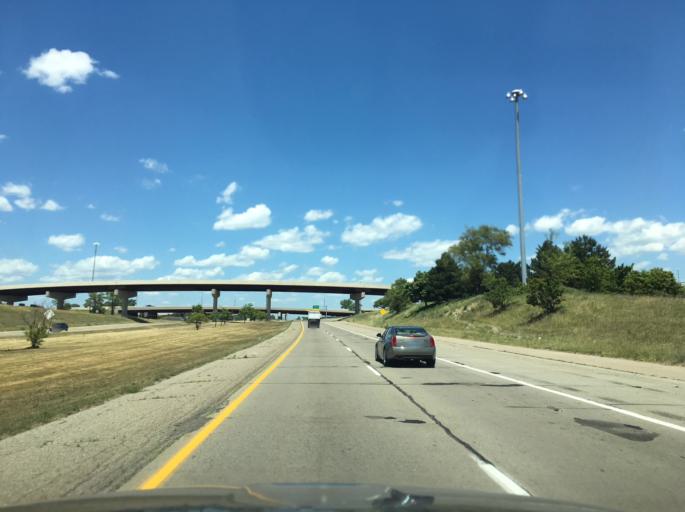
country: US
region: Michigan
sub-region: Macomb County
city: Center Line
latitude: 42.4845
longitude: -83.0453
